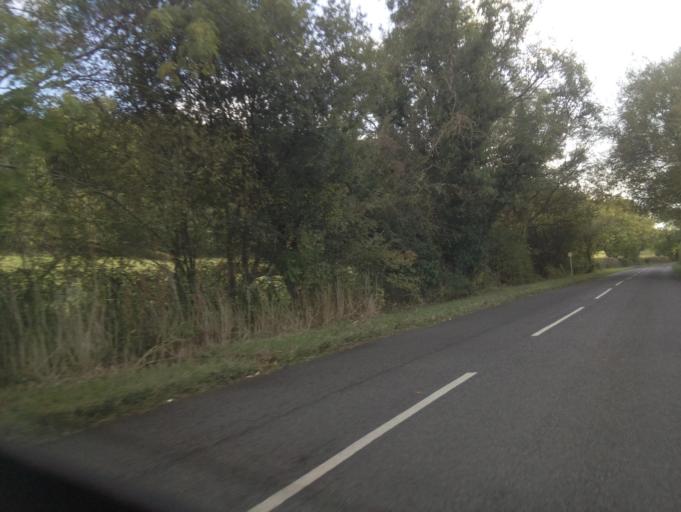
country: GB
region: England
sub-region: South Gloucestershire
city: Severn Beach
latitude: 51.5209
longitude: -2.6433
